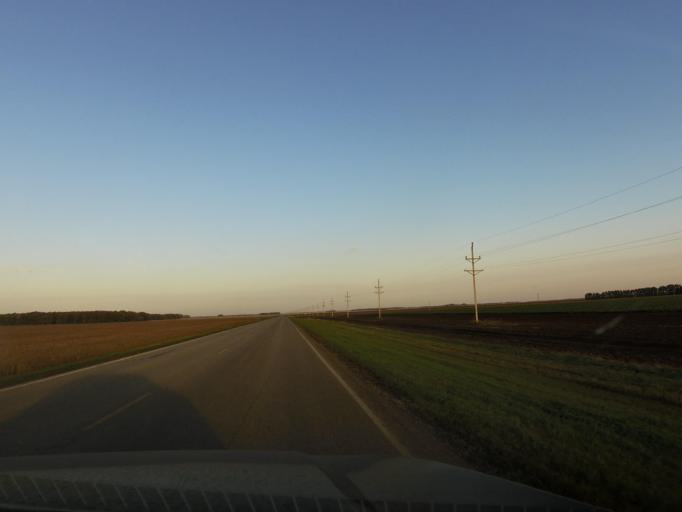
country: CA
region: Manitoba
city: Altona
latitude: 48.9630
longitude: -97.6509
